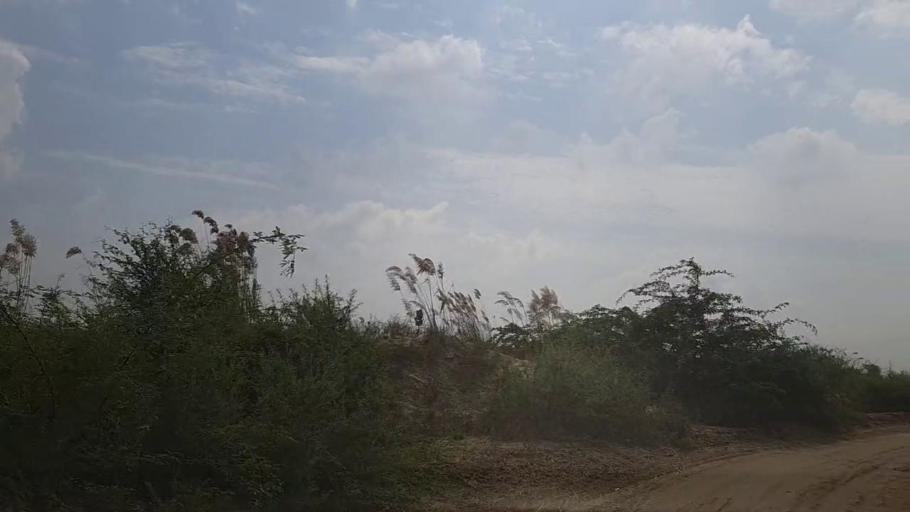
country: PK
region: Sindh
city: Mirpur Batoro
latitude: 24.6060
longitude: 68.1399
